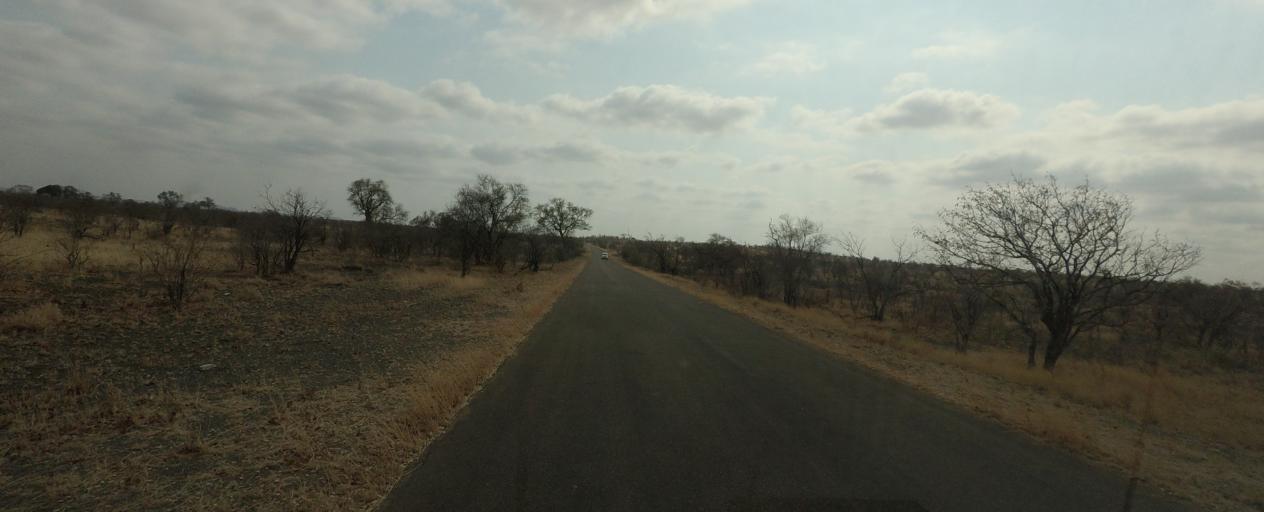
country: ZA
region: Limpopo
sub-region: Vhembe District Municipality
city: Mutale
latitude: -22.5761
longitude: 31.1876
